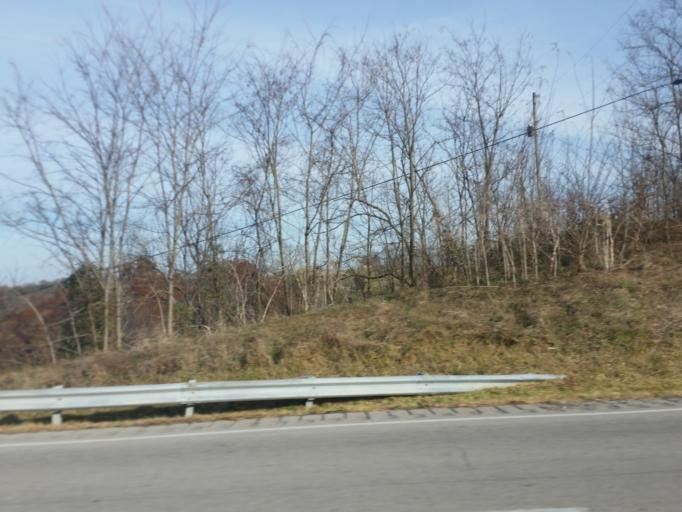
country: US
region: Kentucky
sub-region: Harrison County
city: Cynthiana
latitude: 38.5173
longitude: -84.2895
